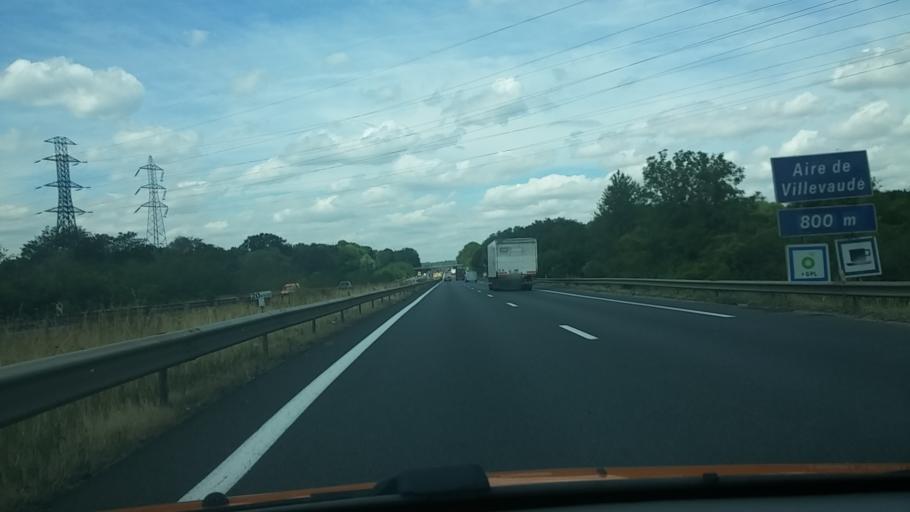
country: FR
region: Ile-de-France
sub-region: Departement de Seine-et-Marne
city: Villevaude
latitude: 48.8988
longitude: 2.6572
